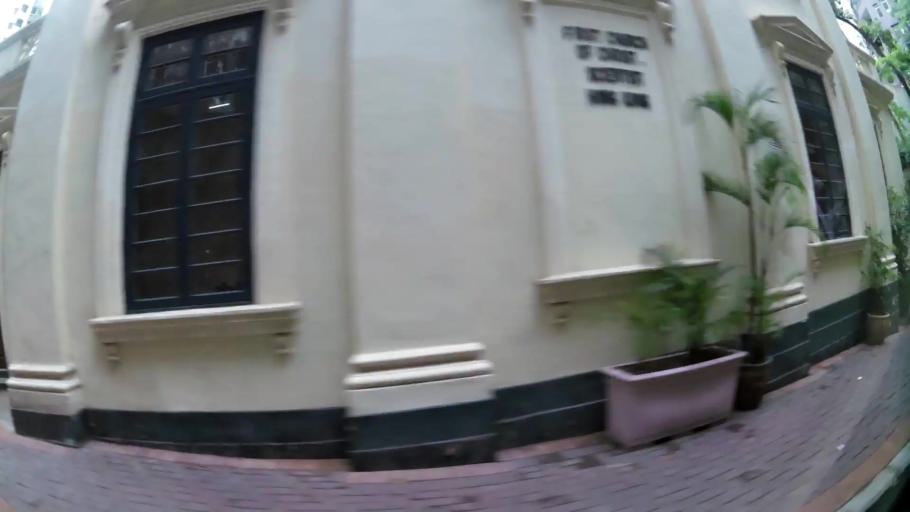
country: HK
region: Central and Western
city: Central
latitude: 22.2752
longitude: 114.1575
